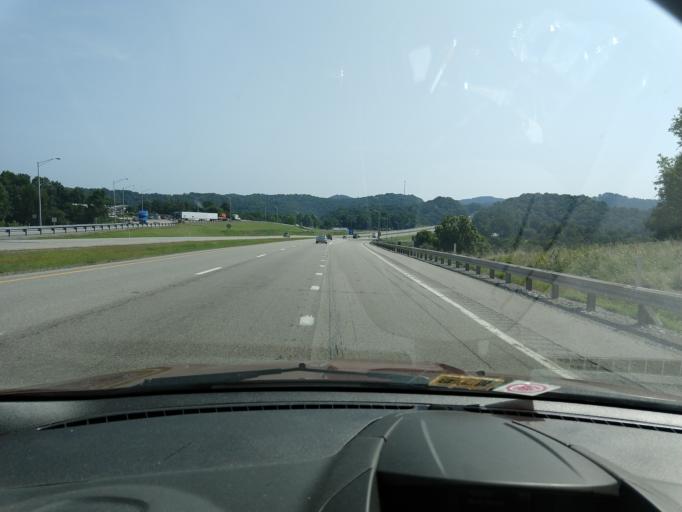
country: US
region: West Virginia
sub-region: Lewis County
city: Weston
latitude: 38.9111
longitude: -80.5978
